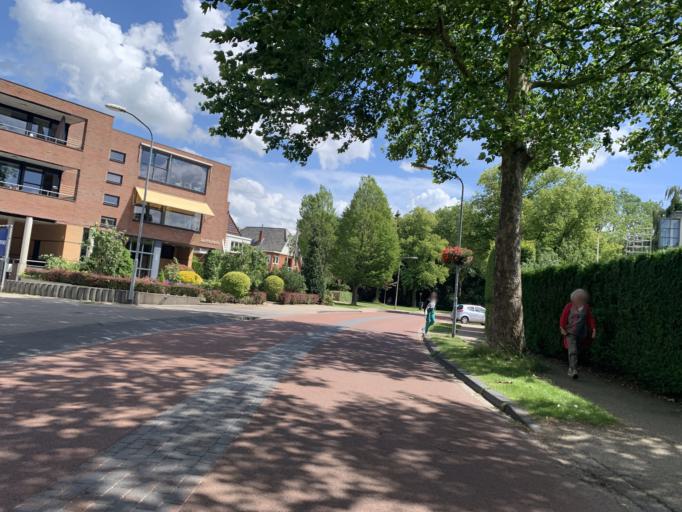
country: NL
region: Groningen
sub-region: Gemeente Haren
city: Haren
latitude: 53.1736
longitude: 6.6093
